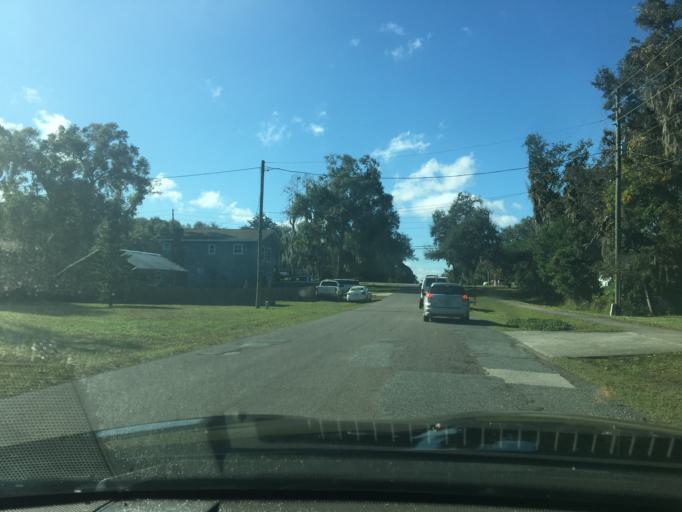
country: US
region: Florida
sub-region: Citrus County
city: Inverness
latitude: 28.8304
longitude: -82.3292
